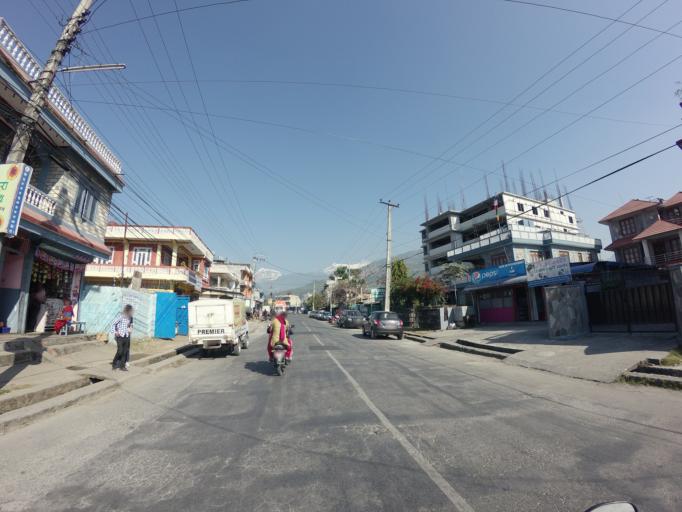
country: NP
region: Western Region
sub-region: Gandaki Zone
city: Pokhara
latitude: 28.2187
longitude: 83.9976
